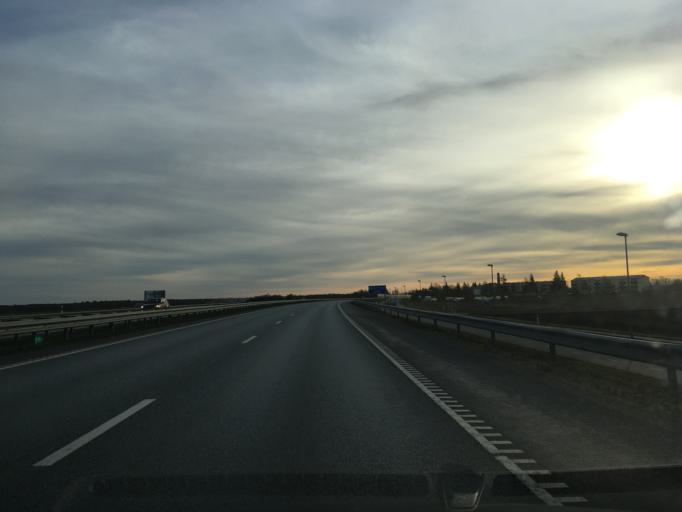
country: EE
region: Ida-Virumaa
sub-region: Johvi vald
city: Johvi
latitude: 59.3822
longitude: 27.3652
